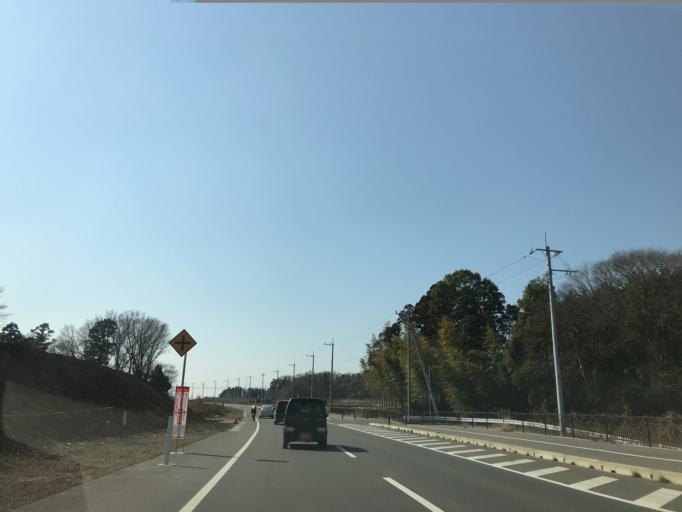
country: JP
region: Ibaraki
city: Mitsukaido
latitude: 36.0124
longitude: 140.0348
